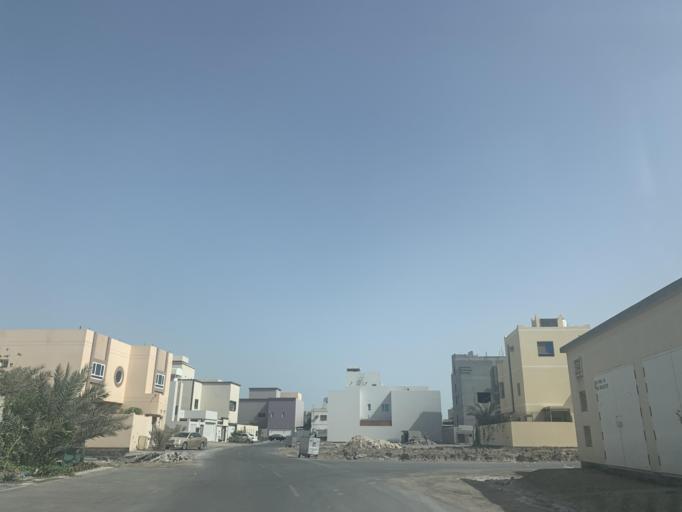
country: BH
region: Northern
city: Sitrah
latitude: 26.1658
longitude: 50.6200
